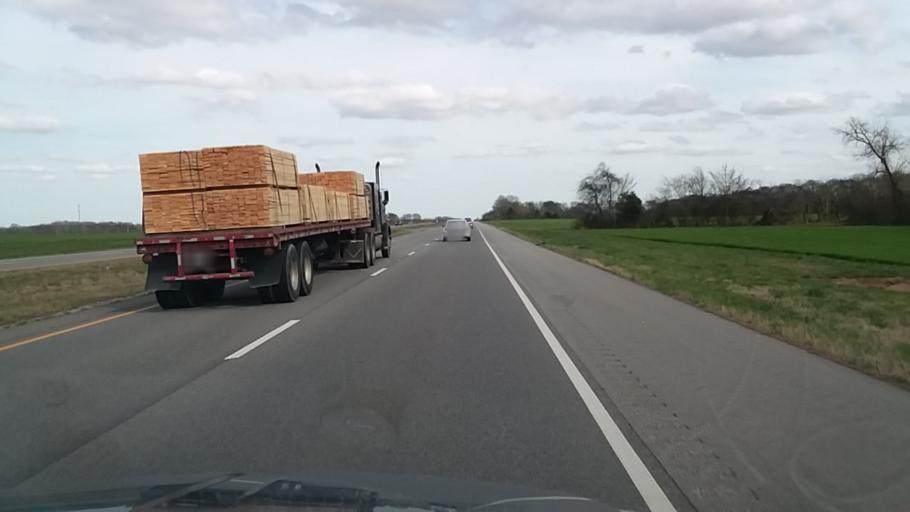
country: US
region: Alabama
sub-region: Lawrence County
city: Town Creek
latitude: 34.6840
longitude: -87.5391
